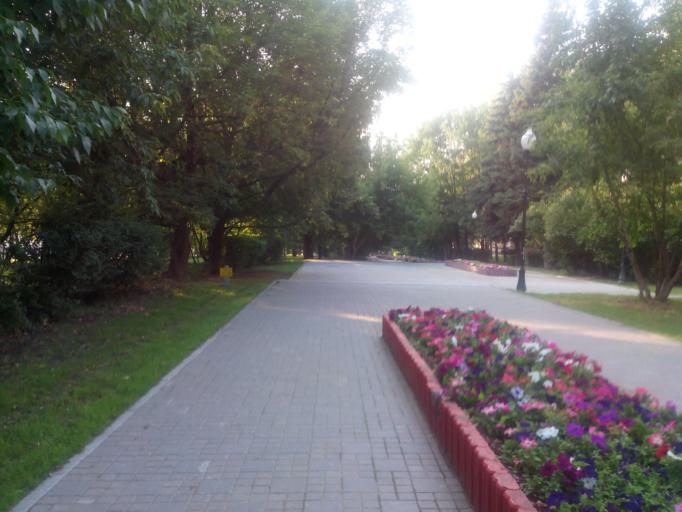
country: RU
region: Moscow
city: Vorob'yovo
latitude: 55.7404
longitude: 37.5209
